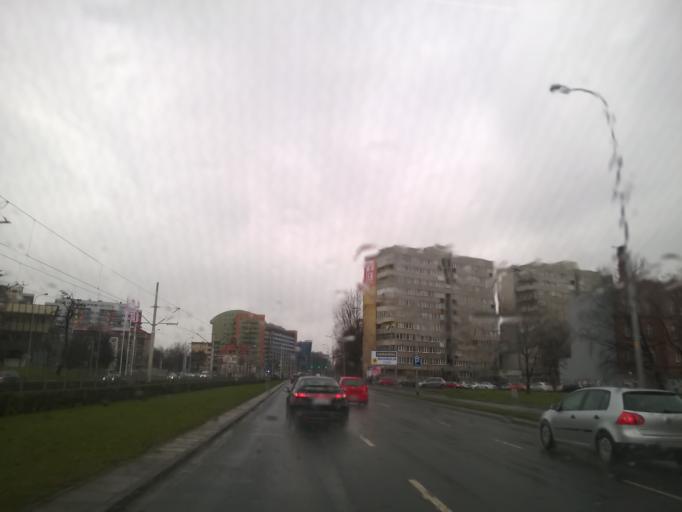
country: PL
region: Lower Silesian Voivodeship
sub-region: Powiat wroclawski
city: Wroclaw
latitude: 51.1136
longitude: 17.0058
